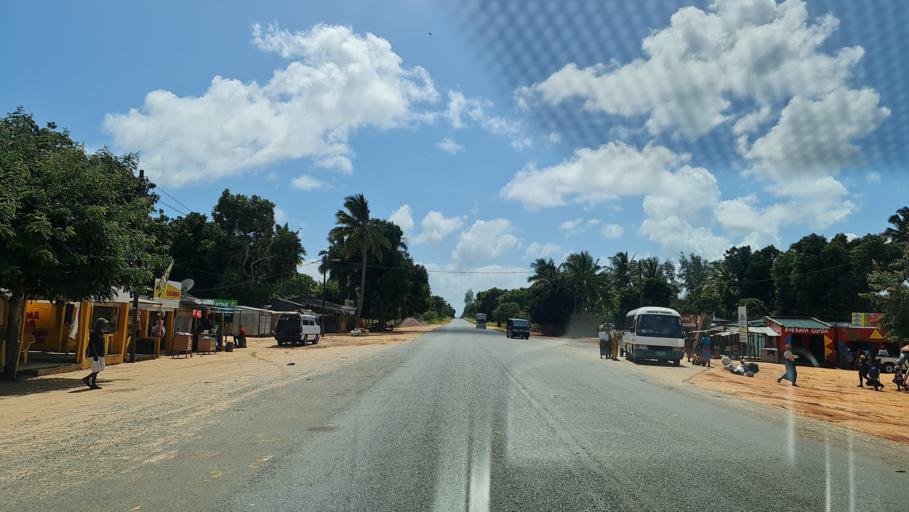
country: MZ
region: Inhambane
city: Maxixe
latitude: -24.5292
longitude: 34.9521
